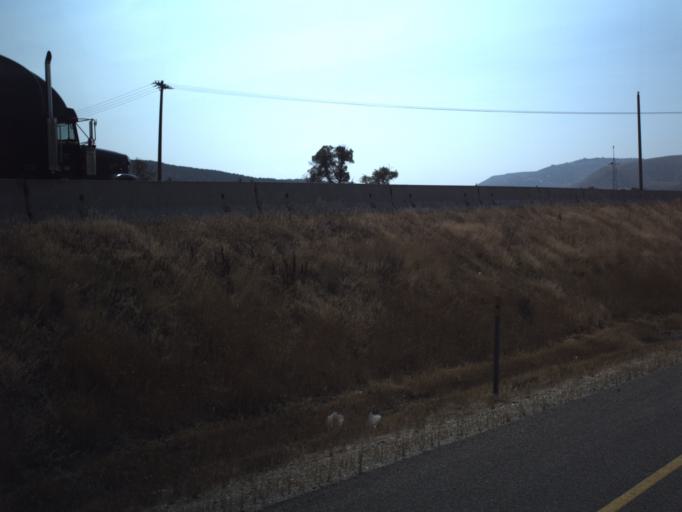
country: US
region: Utah
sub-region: Summit County
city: Coalville
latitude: 40.8140
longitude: -111.4010
